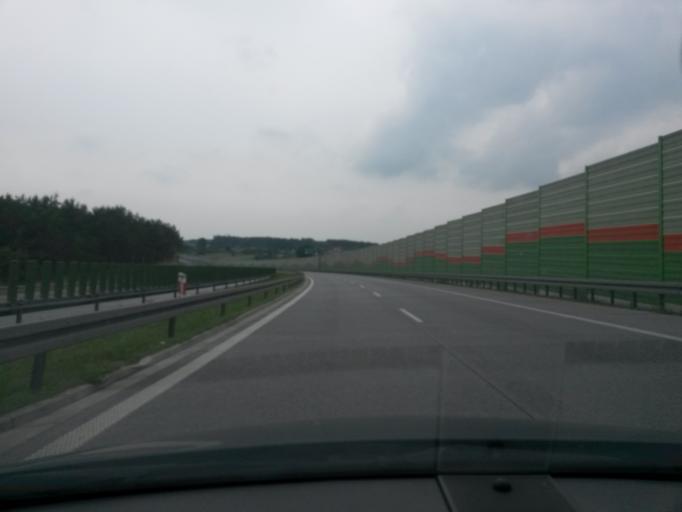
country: PL
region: Lodz Voivodeship
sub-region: Powiat rawski
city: Rawa Mazowiecka
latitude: 51.7136
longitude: 20.2190
